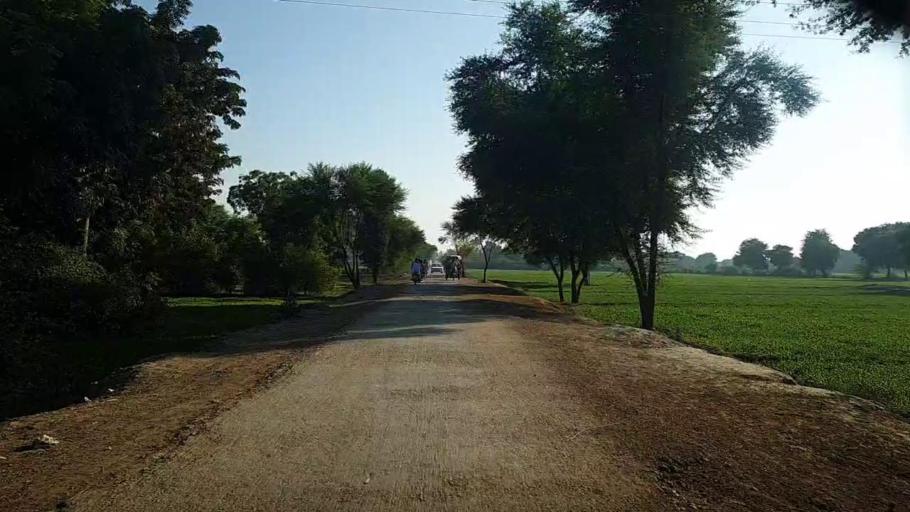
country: PK
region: Sindh
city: Darya Khan Marri
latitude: 26.7001
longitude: 68.3625
